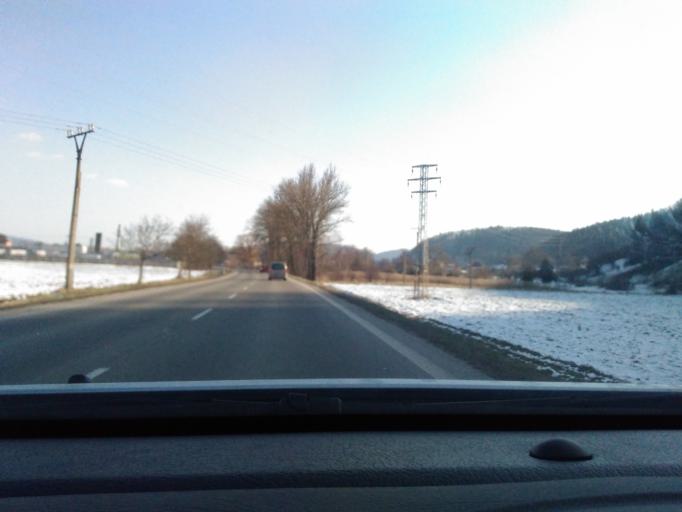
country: CZ
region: South Moravian
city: Tisnov
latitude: 49.3446
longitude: 16.4139
